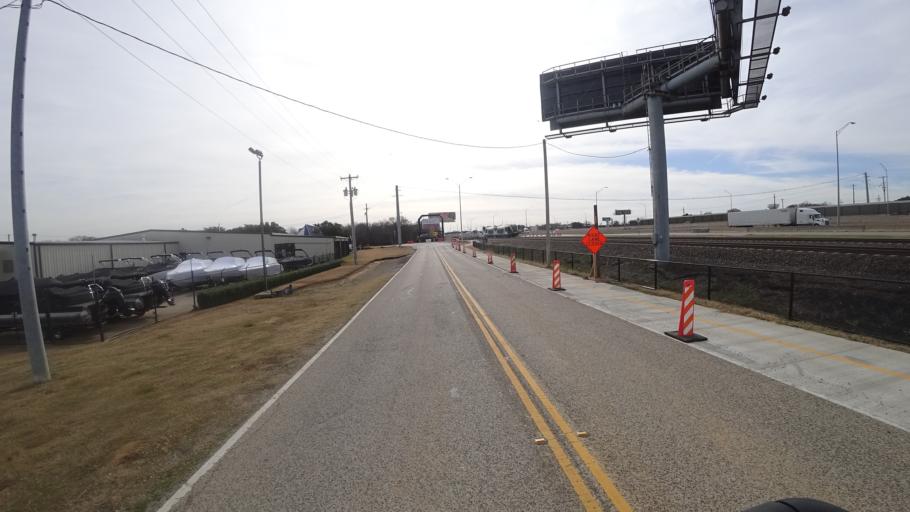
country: US
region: Texas
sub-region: Denton County
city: Highland Village
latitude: 33.0823
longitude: -97.0254
